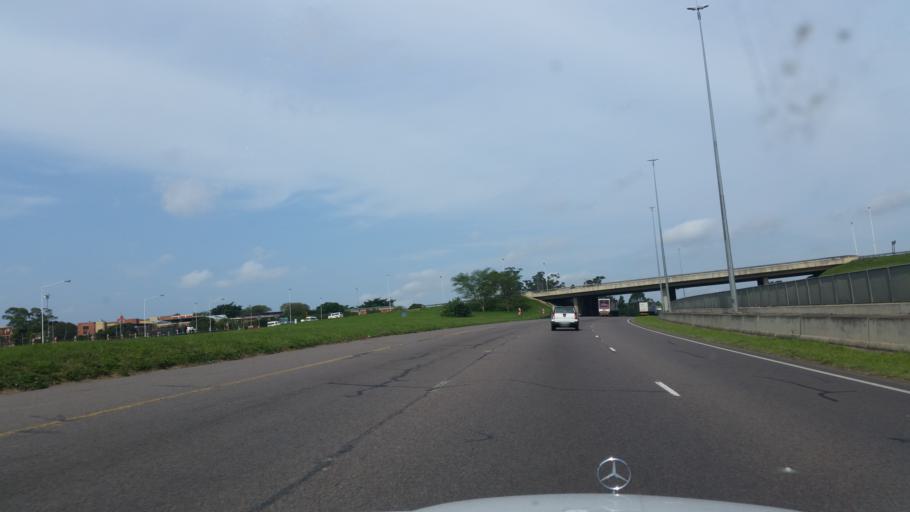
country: ZA
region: KwaZulu-Natal
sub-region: eThekwini Metropolitan Municipality
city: Berea
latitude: -29.8272
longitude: 30.8319
